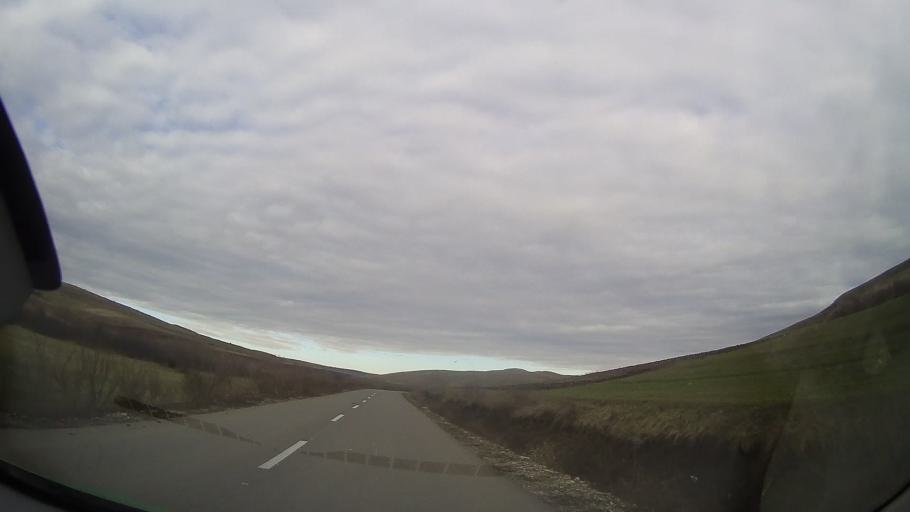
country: RO
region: Bistrita-Nasaud
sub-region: Comuna Silvasu de Campie
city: Silvasu de Campie
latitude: 46.7975
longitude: 24.2960
